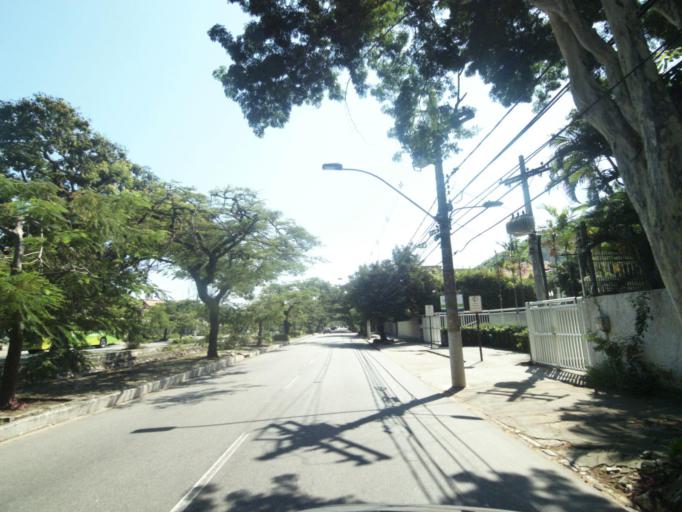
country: BR
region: Rio de Janeiro
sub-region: Niteroi
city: Niteroi
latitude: -22.9140
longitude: -43.0861
